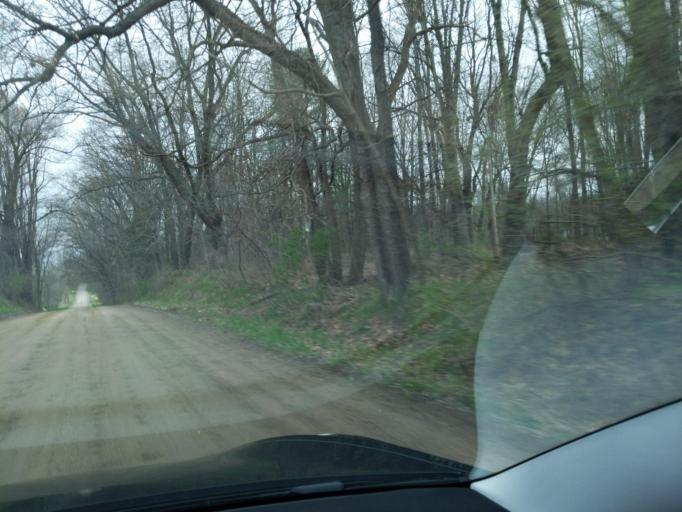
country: US
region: Michigan
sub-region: Ingham County
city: Stockbridge
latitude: 42.4463
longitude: -84.1149
